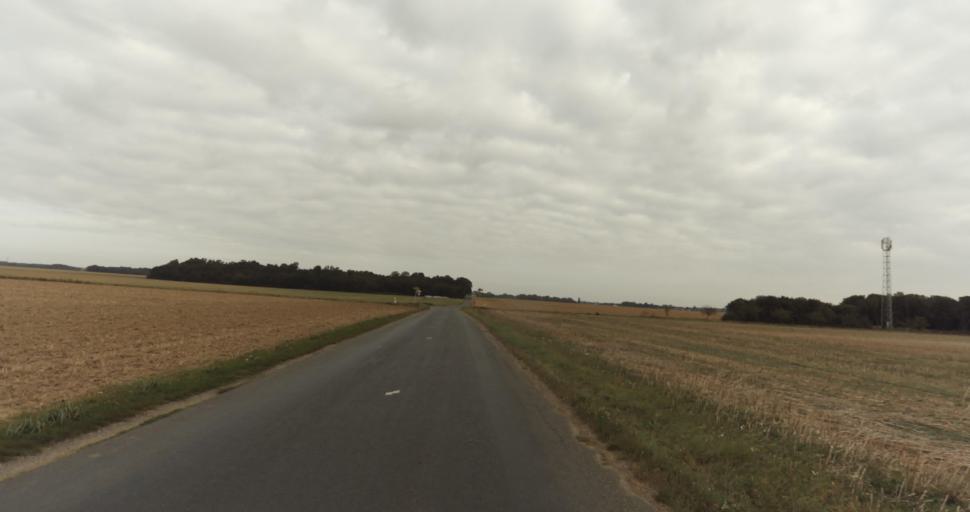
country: FR
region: Haute-Normandie
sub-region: Departement de l'Eure
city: Saint-Germain-sur-Avre
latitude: 48.8051
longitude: 1.2717
